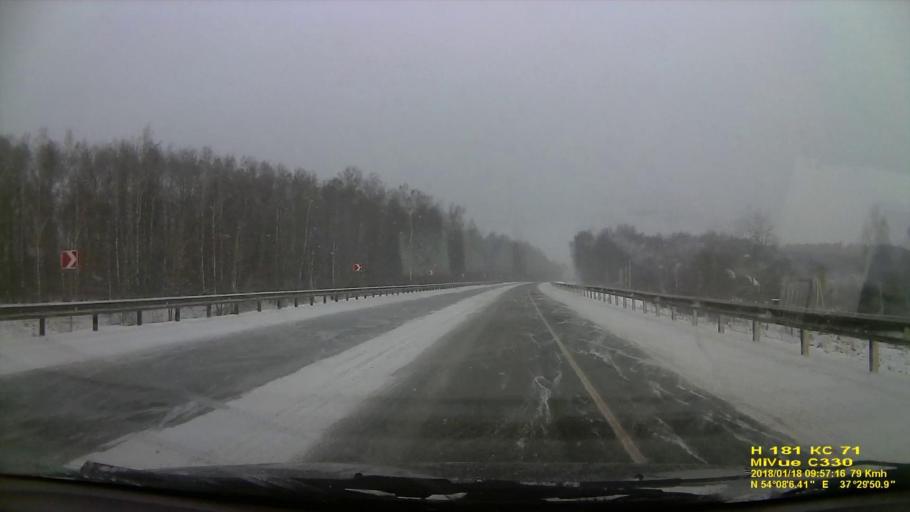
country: RU
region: Tula
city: Kosaya Gora
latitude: 54.1350
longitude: 37.4974
